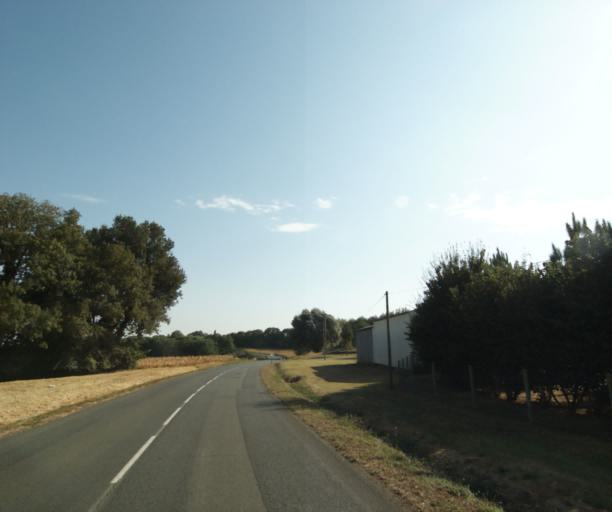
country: FR
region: Poitou-Charentes
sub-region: Departement de la Charente-Maritime
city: Tonnay-Charente
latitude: 45.9591
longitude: -0.8875
